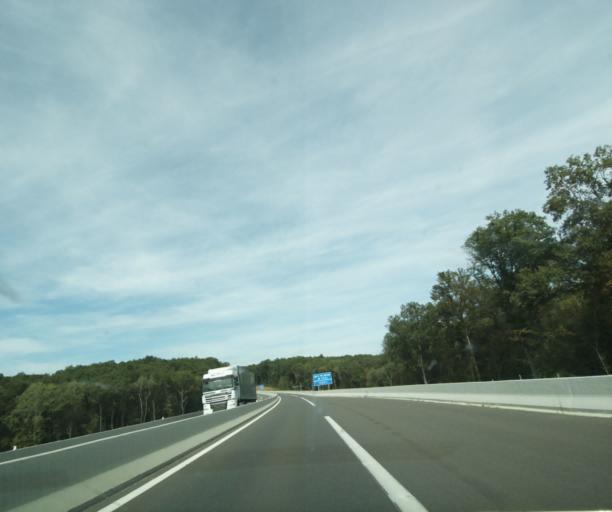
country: FR
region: Auvergne
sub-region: Departement de l'Allier
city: Vendat
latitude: 46.1297
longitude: 3.3625
